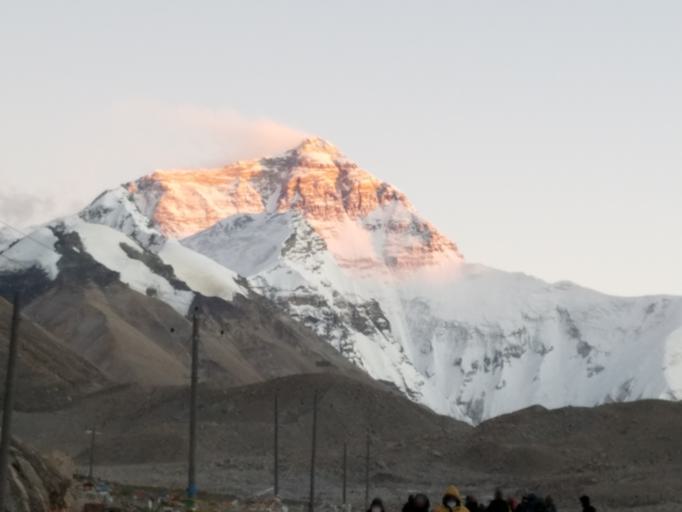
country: NP
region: Eastern Region
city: Lobujya
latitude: 28.1642
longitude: 86.8422
